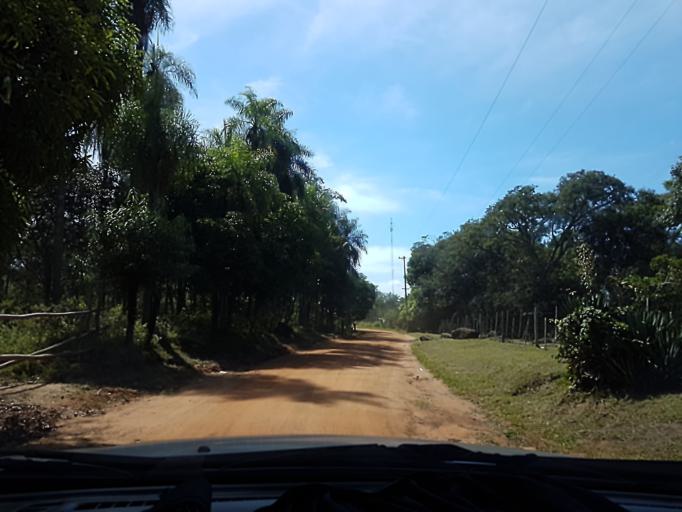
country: PY
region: Cordillera
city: Arroyos y Esteros
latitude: -24.9939
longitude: -57.2146
